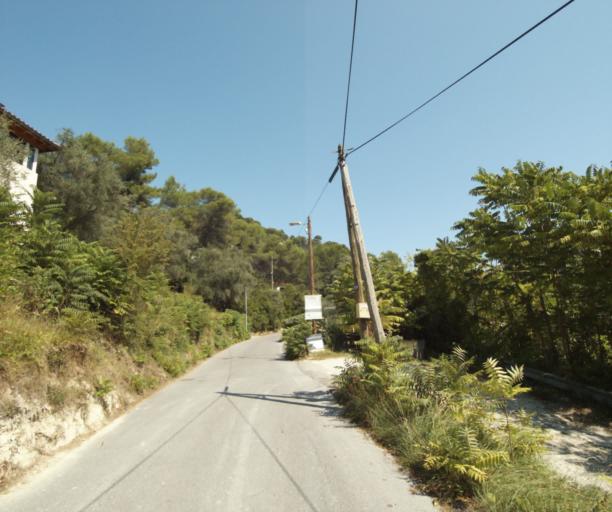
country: FR
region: Provence-Alpes-Cote d'Azur
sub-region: Departement des Alpes-Maritimes
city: Drap
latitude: 43.7543
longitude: 7.3285
